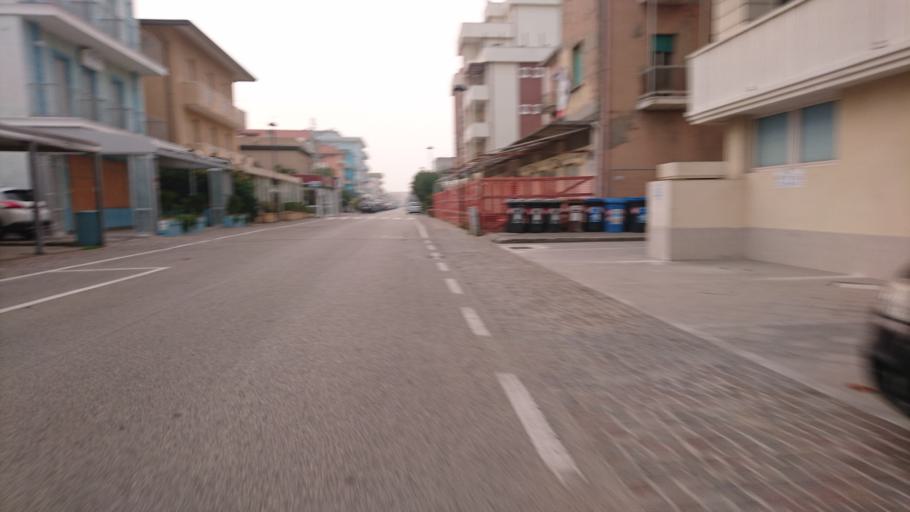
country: IT
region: Emilia-Romagna
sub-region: Provincia di Rimini
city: Rimini
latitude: 44.0761
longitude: 12.5588
